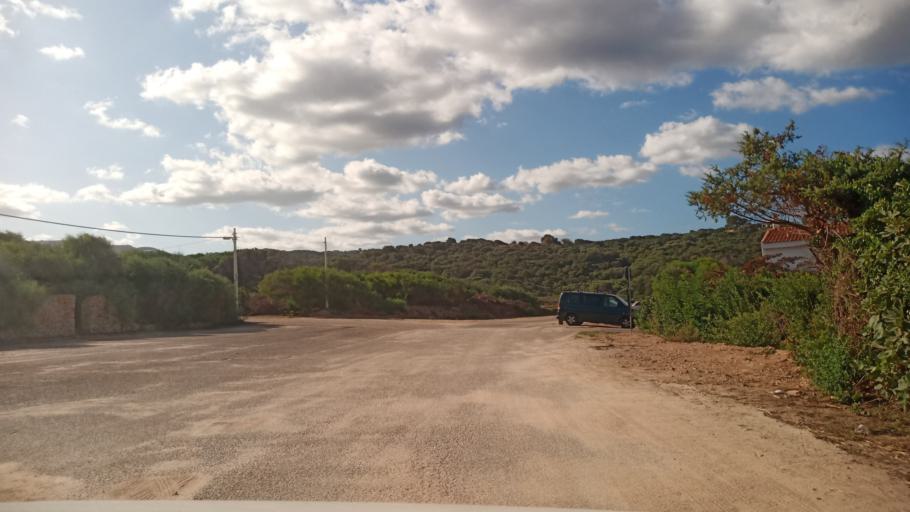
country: IT
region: Sardinia
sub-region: Provincia di Olbia-Tempio
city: Trinita d'Agultu
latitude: 41.0161
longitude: 8.8905
